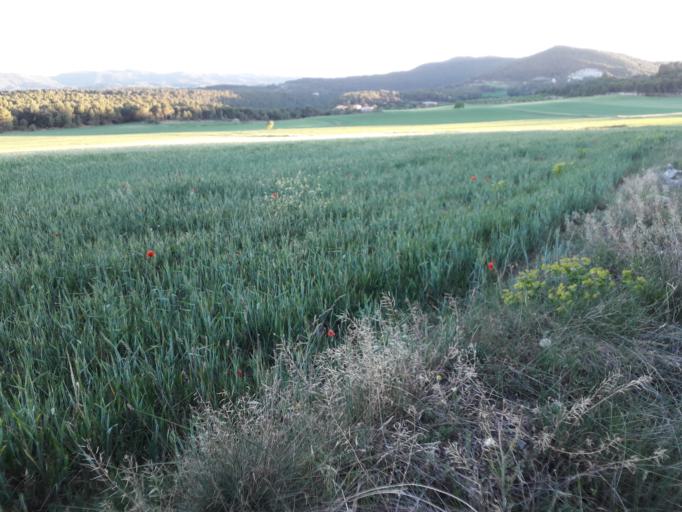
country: ES
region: Catalonia
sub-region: Provincia de Barcelona
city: Jorba
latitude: 41.5921
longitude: 1.5170
